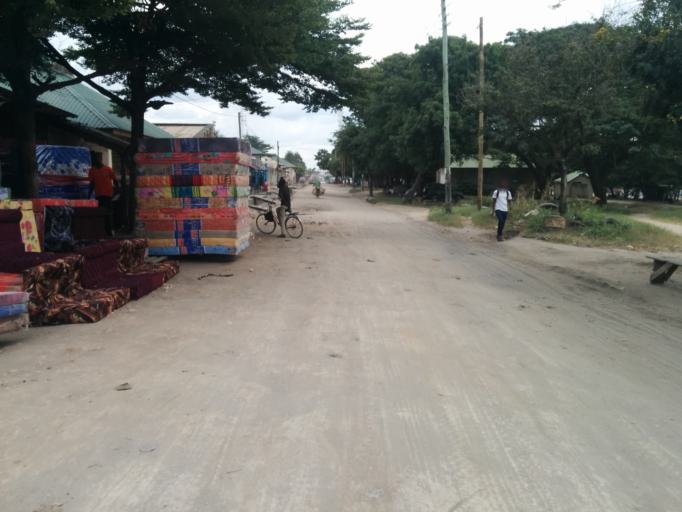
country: TZ
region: Dar es Salaam
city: Dar es Salaam
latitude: -6.8611
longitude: 39.2573
